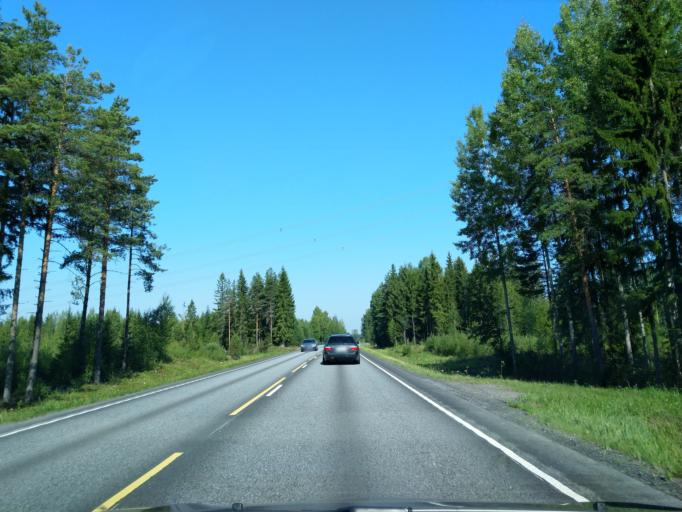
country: FI
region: Satakunta
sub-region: Pori
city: Huittinen
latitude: 61.1458
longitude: 22.7486
